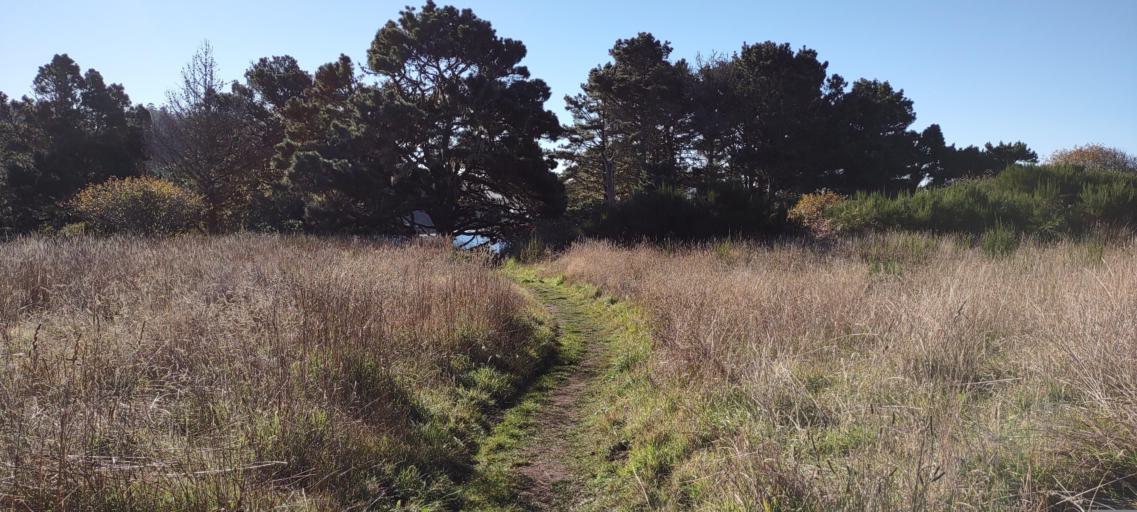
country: US
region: California
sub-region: Mendocino County
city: Fort Bragg
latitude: 39.3043
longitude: -123.7966
